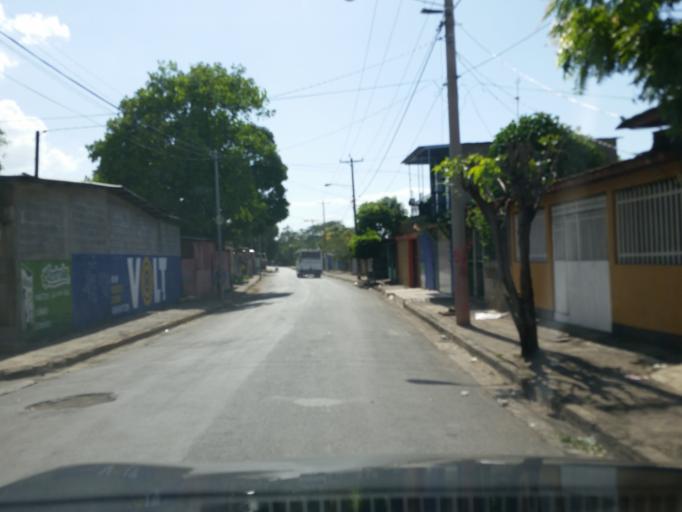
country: NI
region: Managua
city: Managua
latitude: 12.1557
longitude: -86.2206
